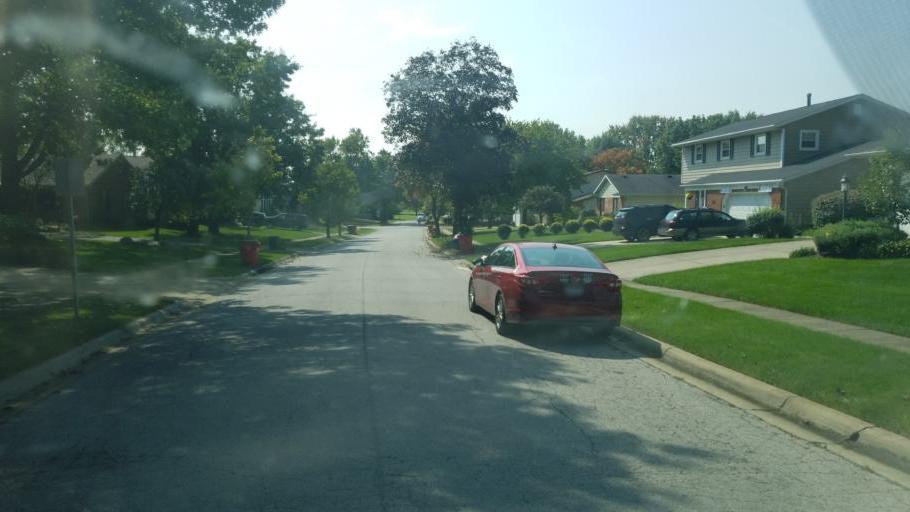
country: US
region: Ohio
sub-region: Franklin County
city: Worthington
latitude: 40.1007
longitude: -83.0193
